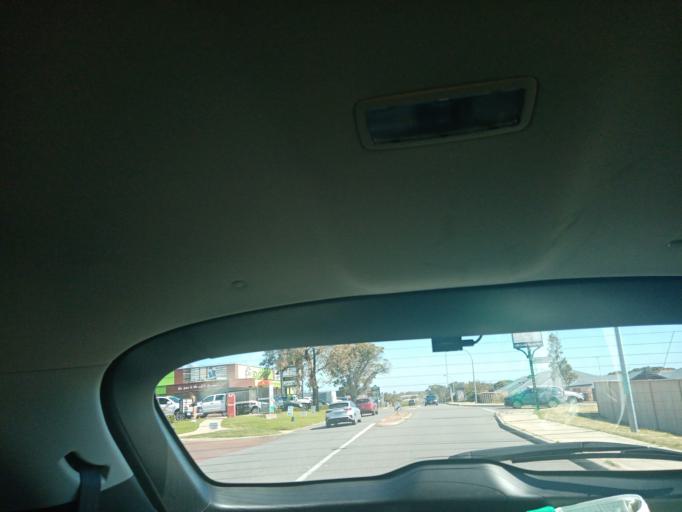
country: AU
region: Western Australia
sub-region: City of Cockburn
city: Spearwood
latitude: -32.1145
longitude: 115.7827
